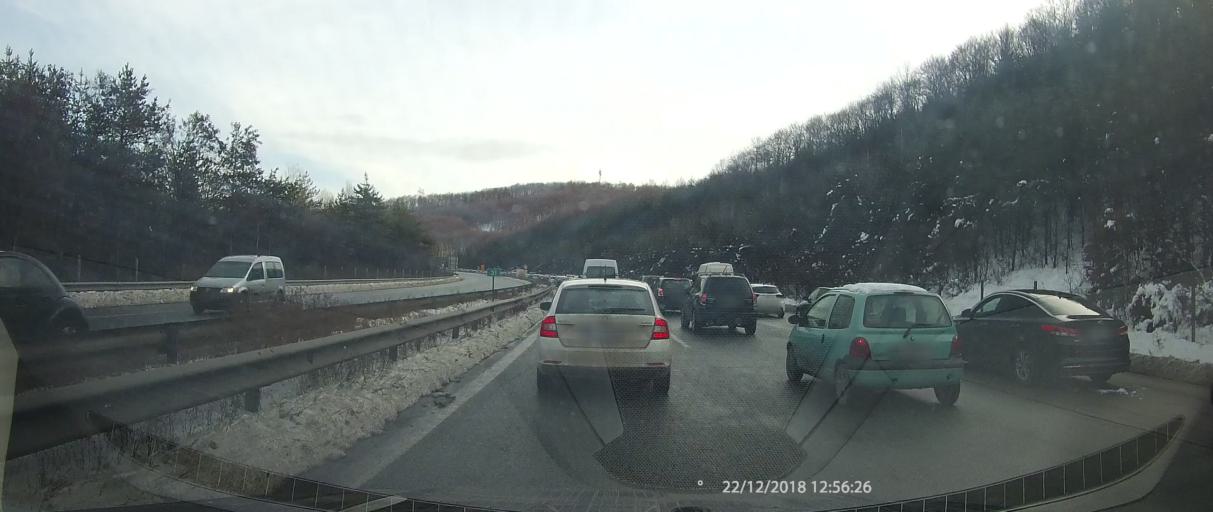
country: BG
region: Sofiya
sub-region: Obshtina Gorna Malina
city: Gorna Malina
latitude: 42.7741
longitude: 23.7812
